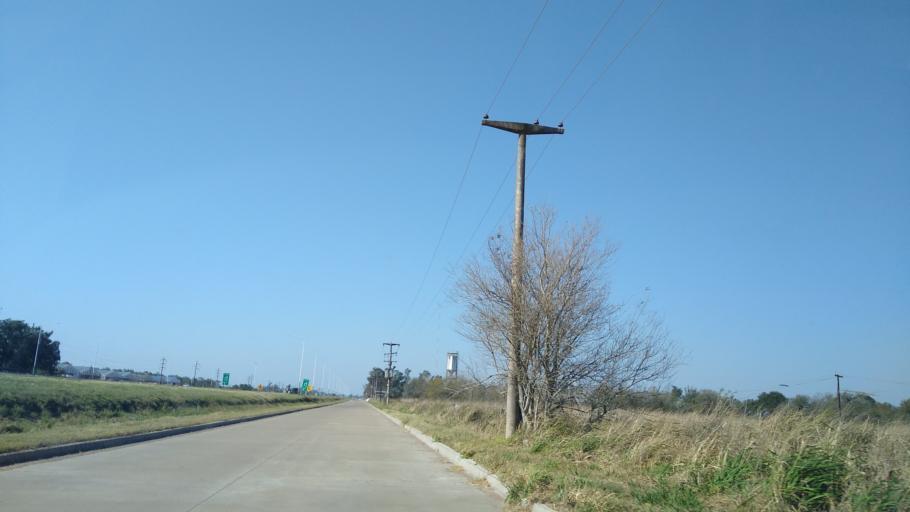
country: AR
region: Chaco
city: Puerto Tirol
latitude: -27.3737
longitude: -59.0489
